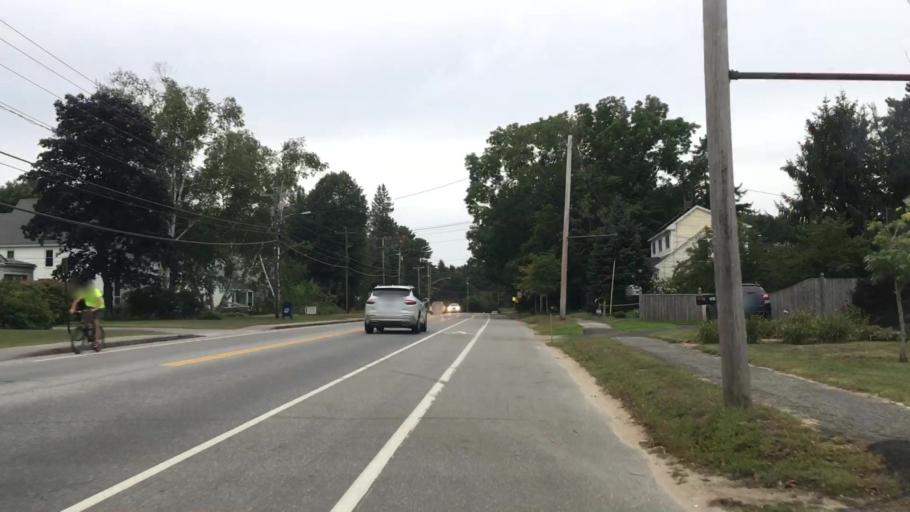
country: US
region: Maine
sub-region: Cumberland County
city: Brunswick
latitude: 43.9016
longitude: -69.9672
